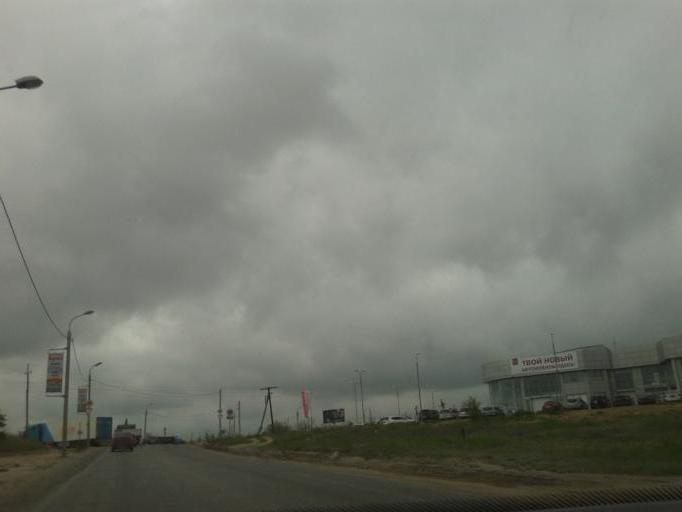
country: RU
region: Volgograd
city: Volgograd
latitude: 48.7054
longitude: 44.4399
